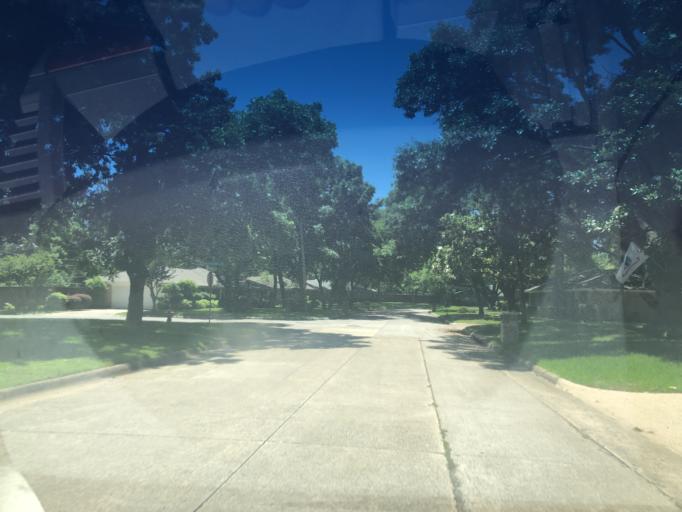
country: US
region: Texas
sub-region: Dallas County
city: Grand Prairie
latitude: 32.7741
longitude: -97.0357
